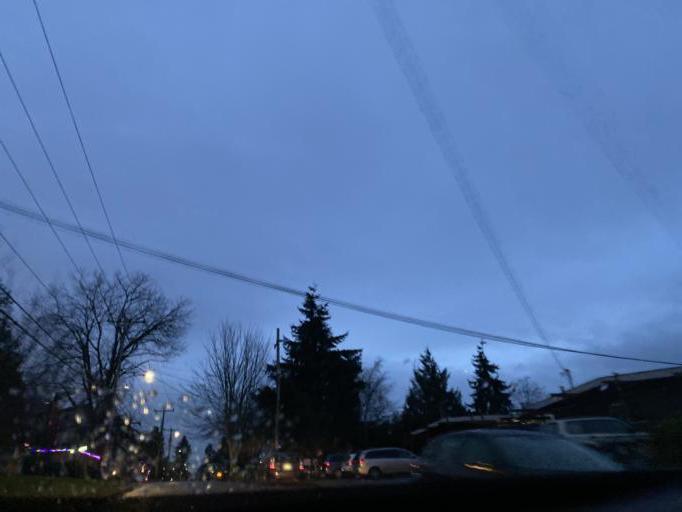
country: US
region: Washington
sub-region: King County
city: Seattle
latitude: 47.6509
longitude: -122.3750
